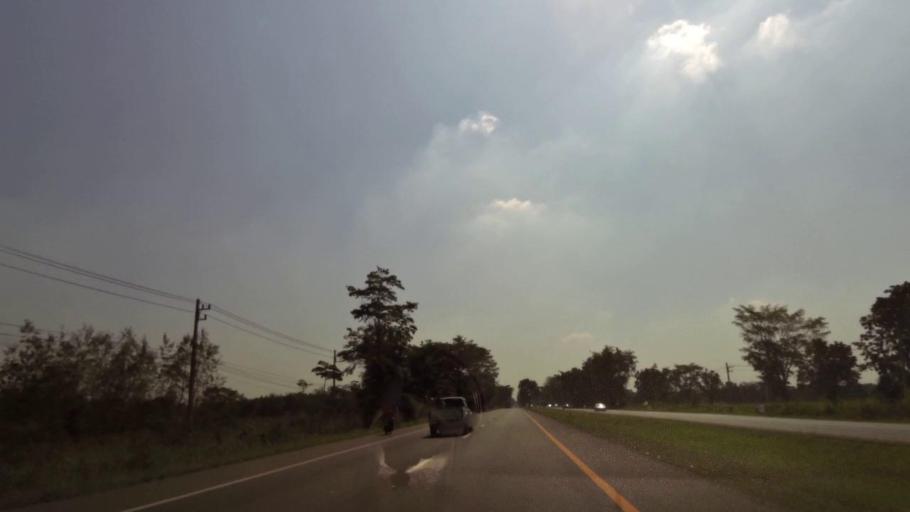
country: TH
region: Phichit
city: Bueng Na Rang
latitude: 16.2261
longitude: 100.1261
